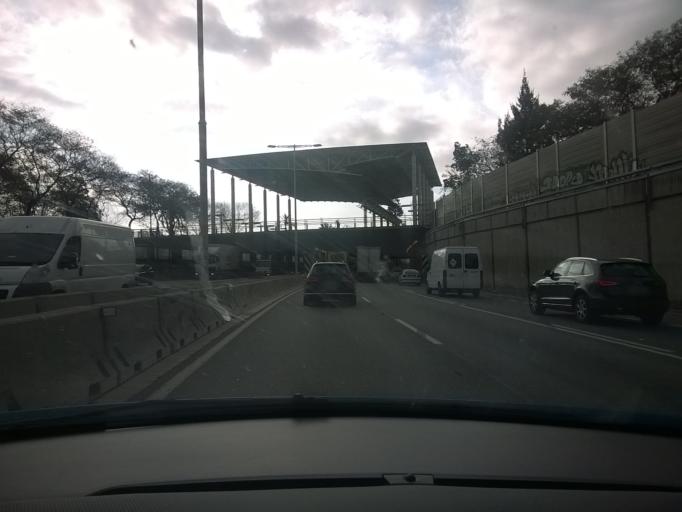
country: ES
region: Catalonia
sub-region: Provincia de Barcelona
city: Santa Coloma de Gramenet
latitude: 41.4484
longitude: 2.2013
